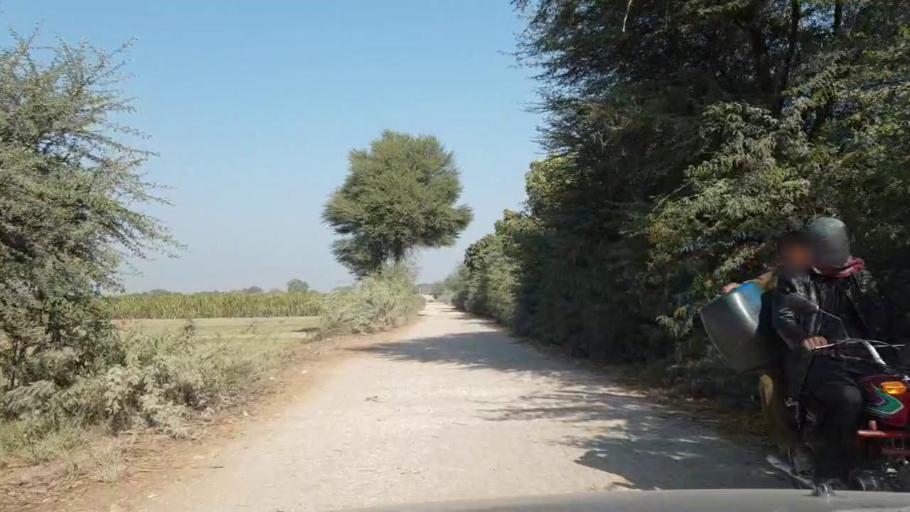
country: PK
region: Sindh
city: Tando Allahyar
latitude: 25.5680
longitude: 68.6080
